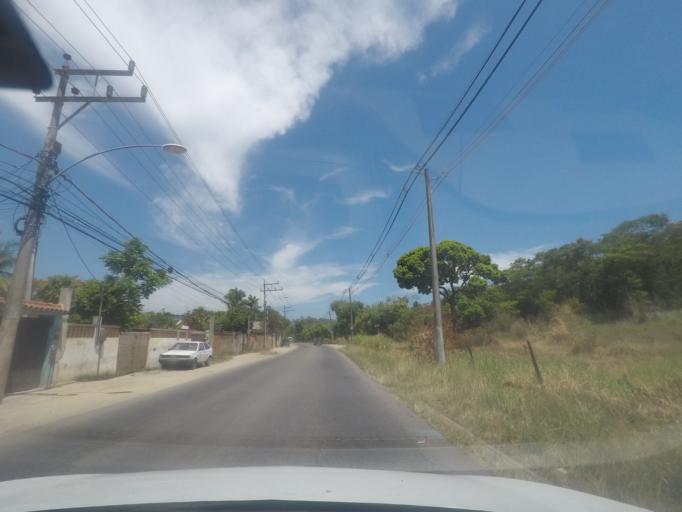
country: BR
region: Rio de Janeiro
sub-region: Itaguai
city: Itaguai
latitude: -22.9861
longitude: -43.6551
